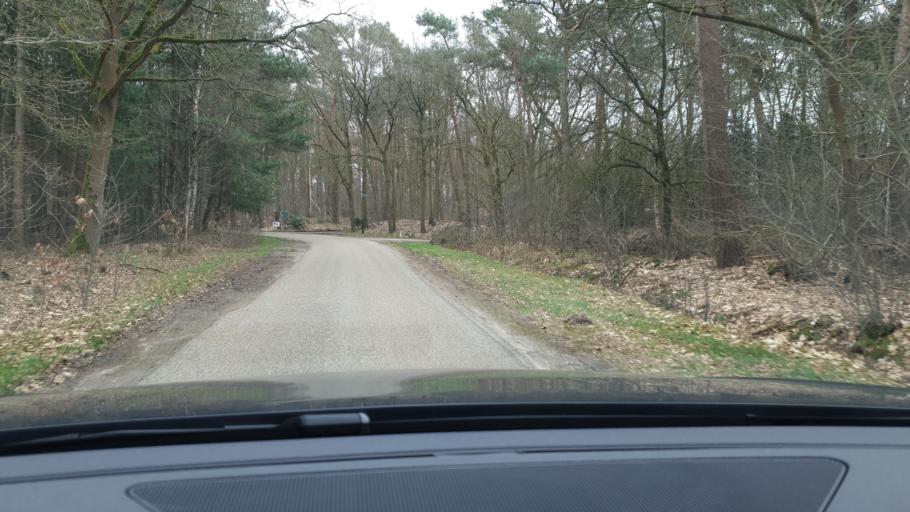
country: NL
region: North Brabant
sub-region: Gemeente Oirschot
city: Oostelbeers
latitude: 51.4218
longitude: 5.3013
